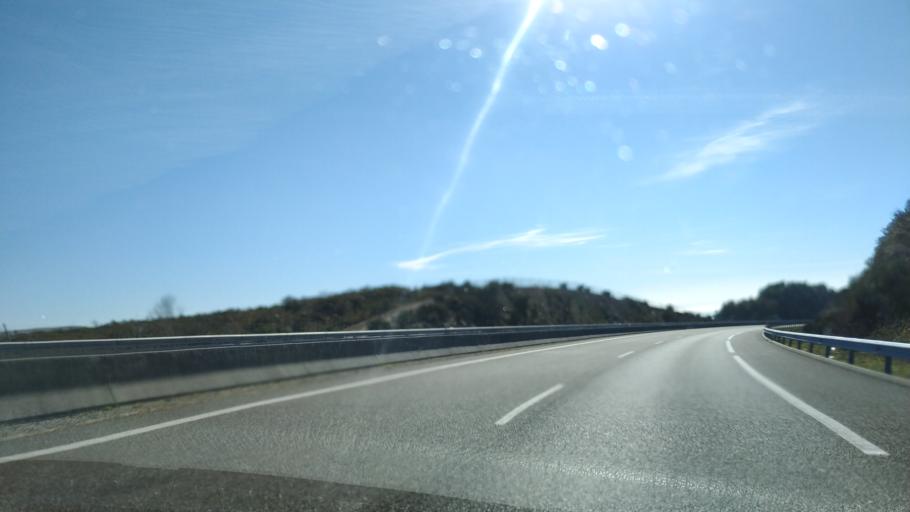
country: ES
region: Galicia
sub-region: Provincia de Pontevedra
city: Dozon
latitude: 42.5530
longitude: -8.0188
